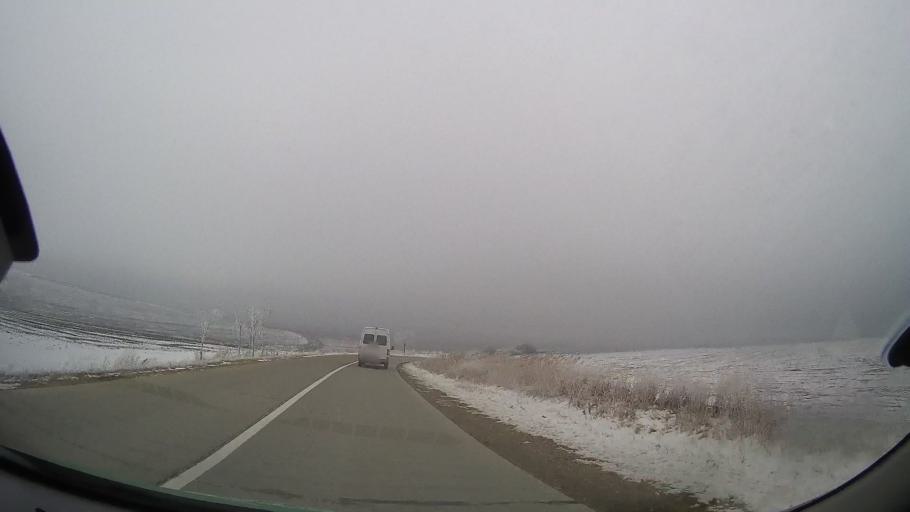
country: RO
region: Vaslui
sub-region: Comuna Ivesti
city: Ivesti
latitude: 46.1955
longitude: 27.5999
